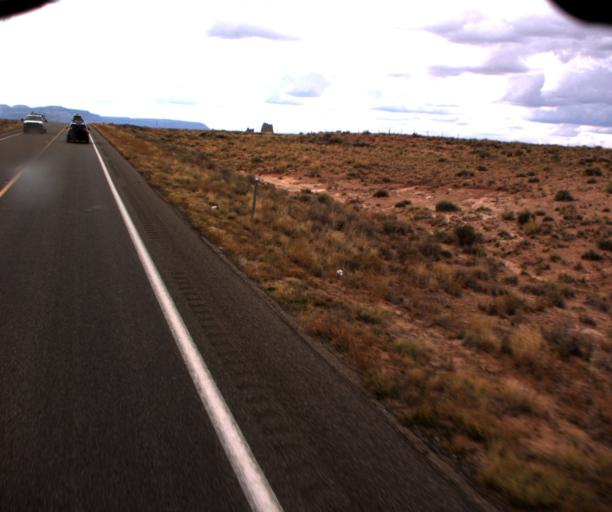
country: US
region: Arizona
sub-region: Navajo County
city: Kayenta
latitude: 36.7418
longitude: -110.0786
